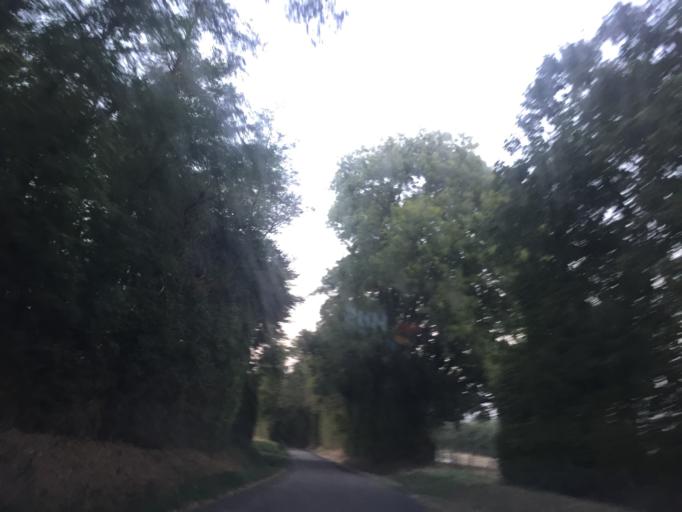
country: FR
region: Rhone-Alpes
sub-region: Departement de l'Ain
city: Saint-Maurice-de-Beynost
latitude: 45.8502
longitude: 4.9732
